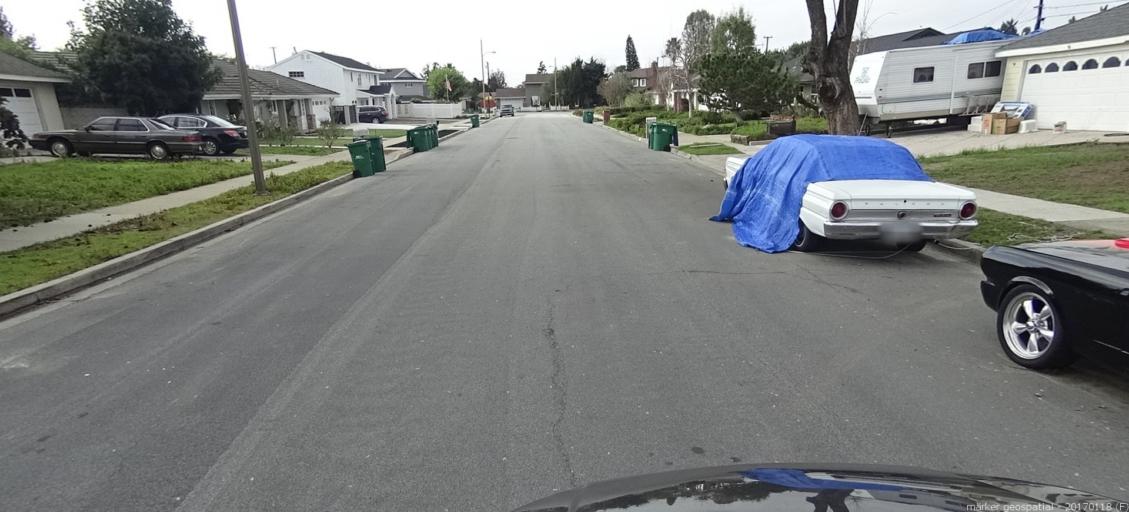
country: US
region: California
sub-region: Orange County
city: North Tustin
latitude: 33.7605
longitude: -117.7968
